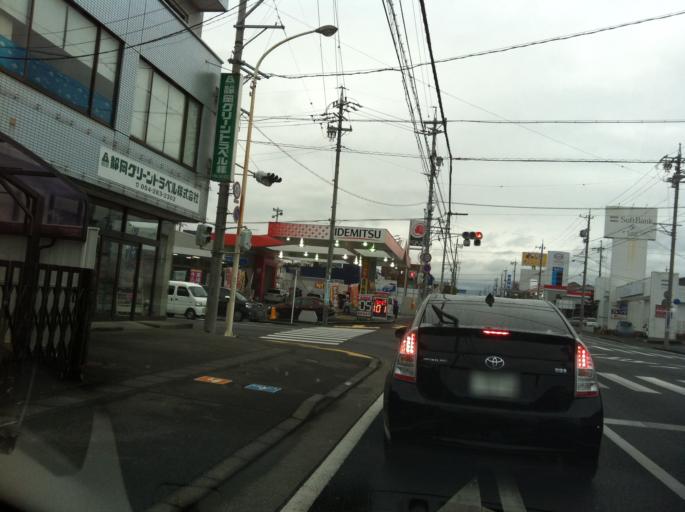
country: JP
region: Shizuoka
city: Shizuoka-shi
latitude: 34.9944
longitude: 138.4345
